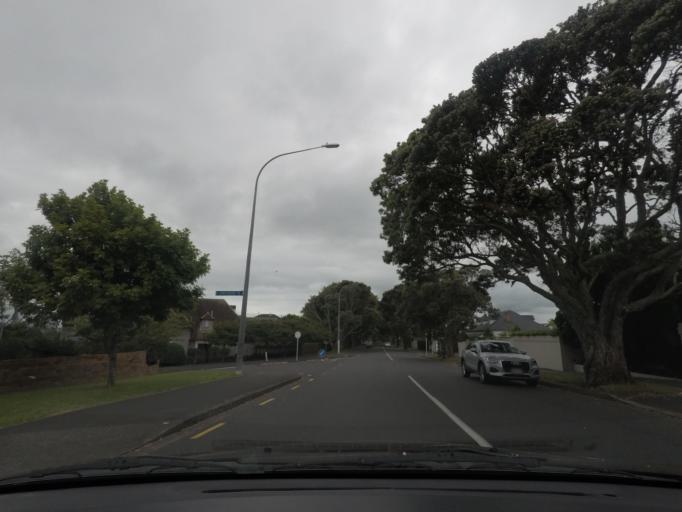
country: NZ
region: Auckland
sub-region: Auckland
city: Auckland
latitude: -36.8543
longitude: 174.7888
